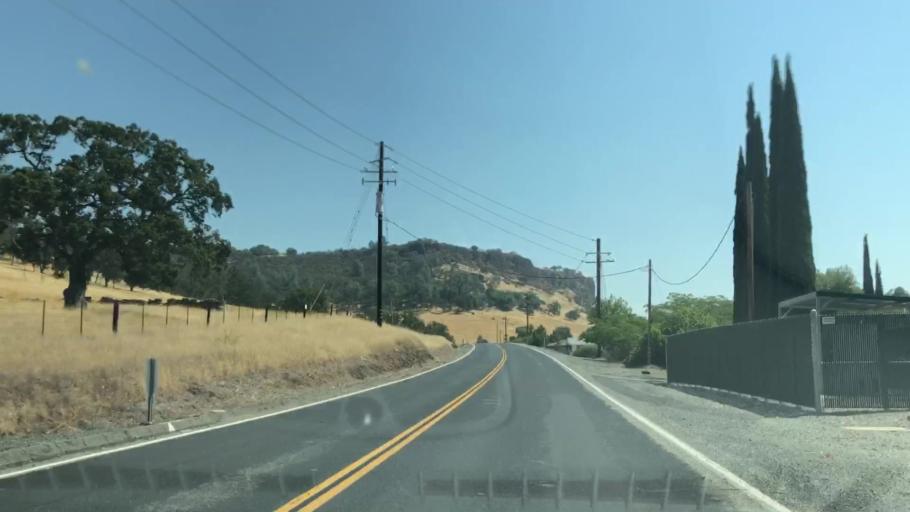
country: US
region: California
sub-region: Calaveras County
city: Copperopolis
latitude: 37.9061
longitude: -120.5853
